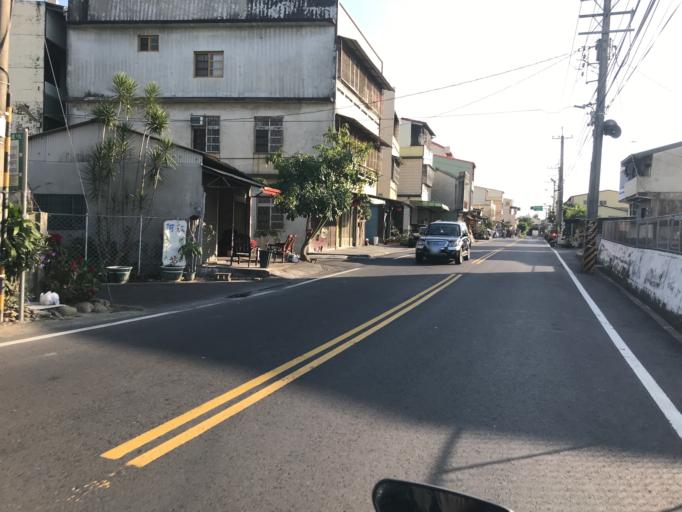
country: TW
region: Taiwan
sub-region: Nantou
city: Nantou
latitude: 23.8683
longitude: 120.6033
